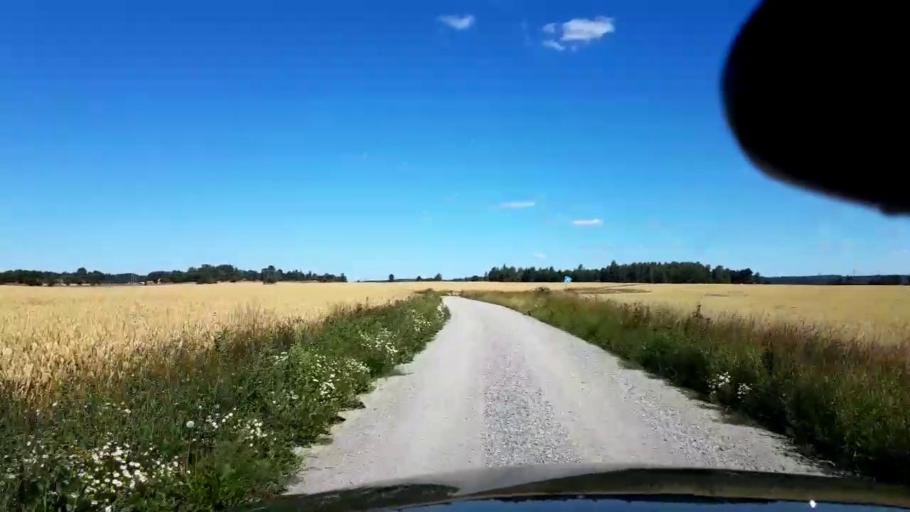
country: SE
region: Stockholm
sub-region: Upplands-Bro Kommun
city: Bro
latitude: 59.5887
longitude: 17.6373
